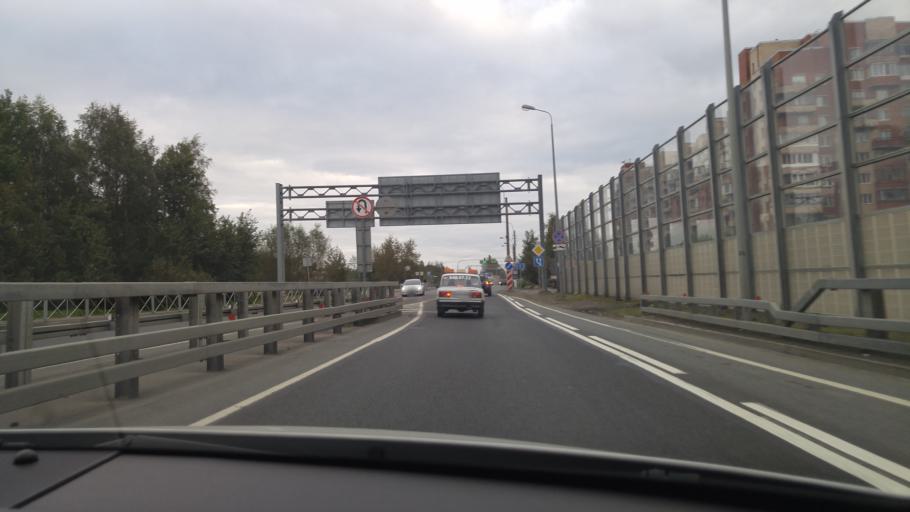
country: RU
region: St.-Petersburg
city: Kronshtadt
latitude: 60.0119
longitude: 29.7237
